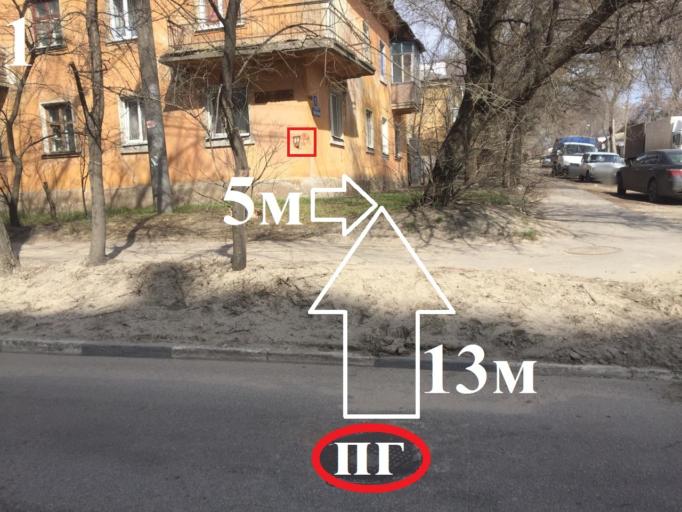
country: RU
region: Voronezj
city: Voronezh
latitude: 51.6945
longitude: 39.1657
